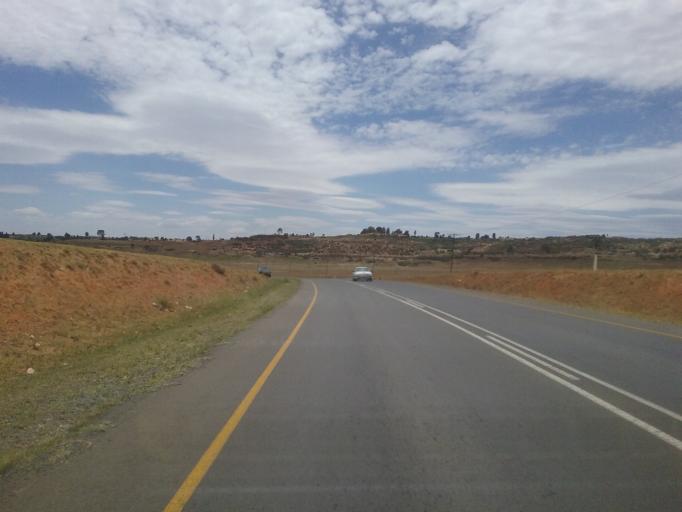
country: LS
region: Maseru
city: Maseru
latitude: -29.5055
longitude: 27.5277
